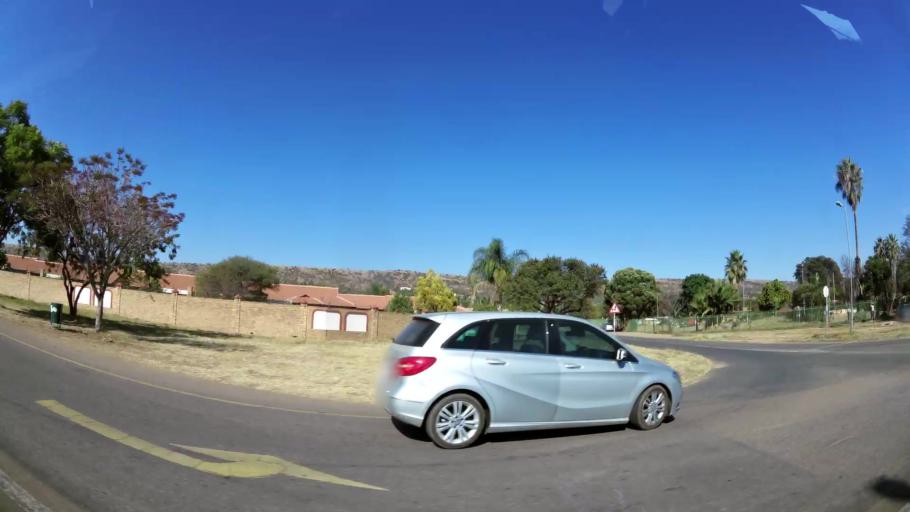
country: ZA
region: Gauteng
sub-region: City of Tshwane Metropolitan Municipality
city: Pretoria
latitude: -25.6825
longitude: 28.2281
